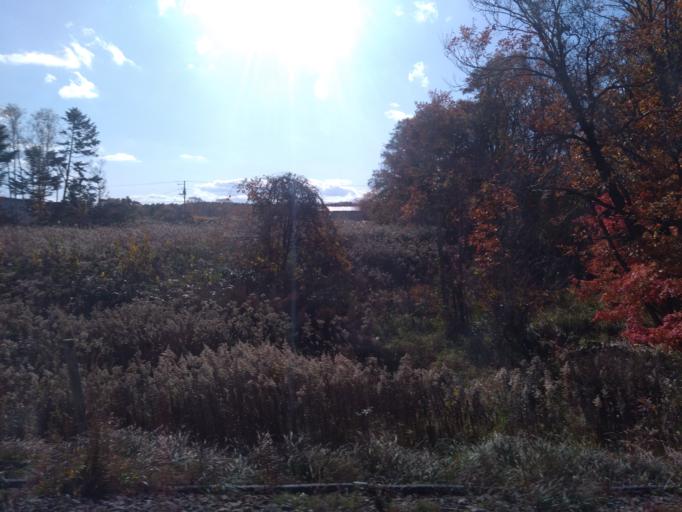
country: JP
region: Hokkaido
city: Kitahiroshima
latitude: 42.9935
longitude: 141.5518
